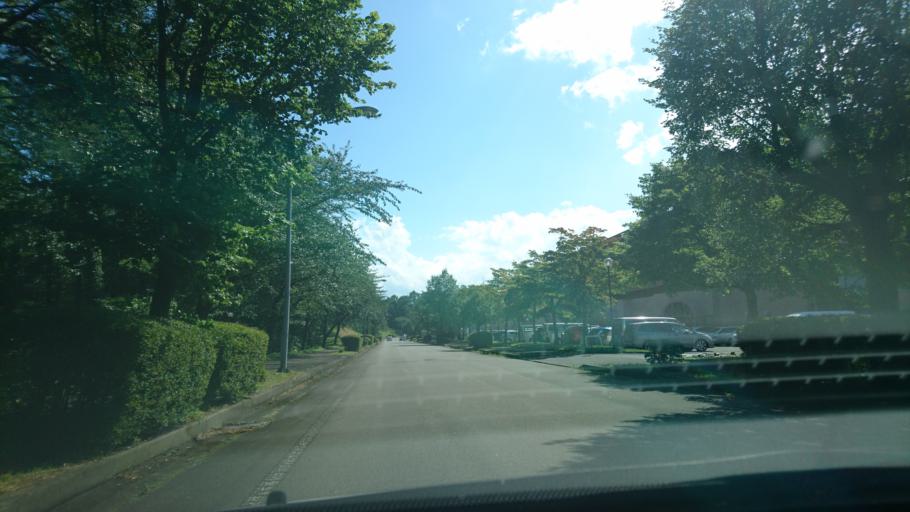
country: JP
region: Iwate
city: Morioka-shi
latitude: 39.8092
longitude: 141.1332
